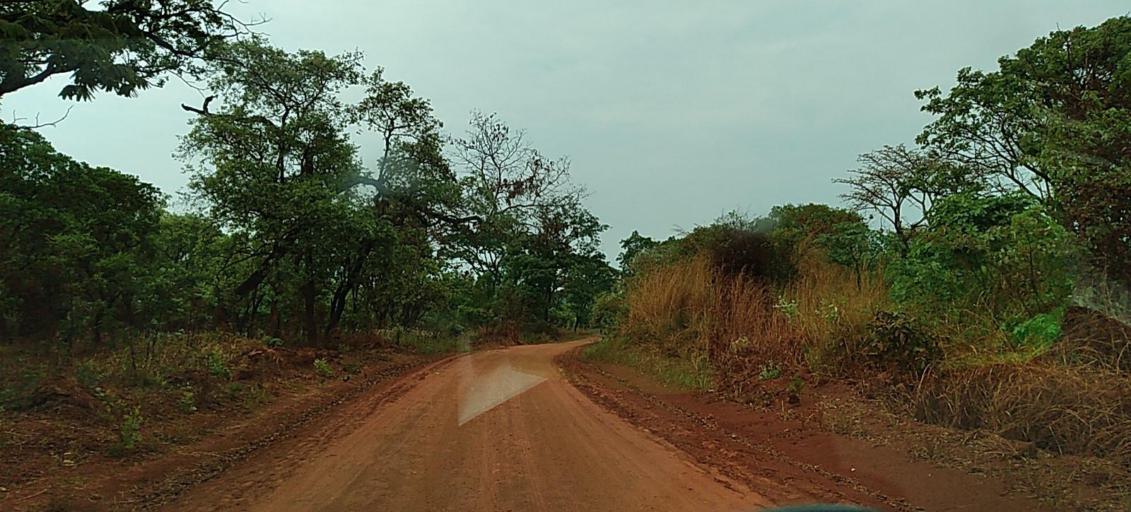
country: ZM
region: North-Western
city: Solwezi
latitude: -12.2217
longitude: 26.5103
